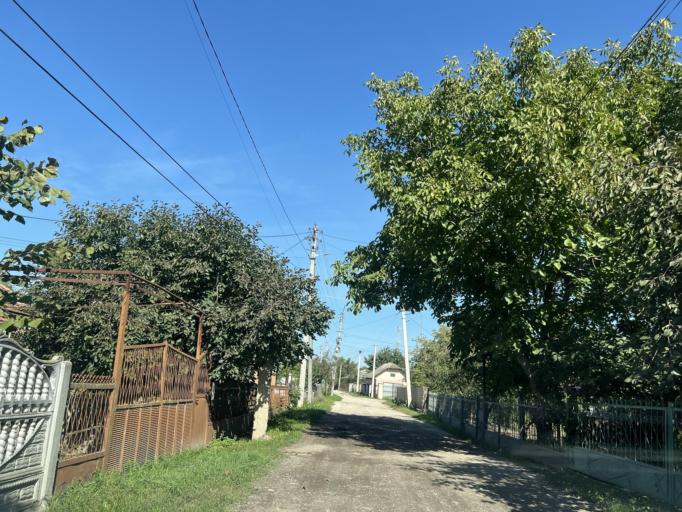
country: RO
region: Iasi
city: Ungheni-Prut
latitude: 47.1944
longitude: 27.7917
